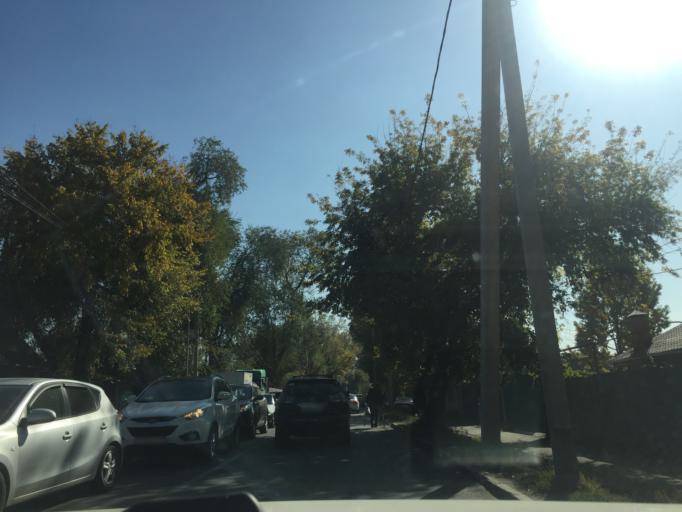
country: KZ
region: Almaty Qalasy
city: Almaty
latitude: 43.2657
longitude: 76.9105
